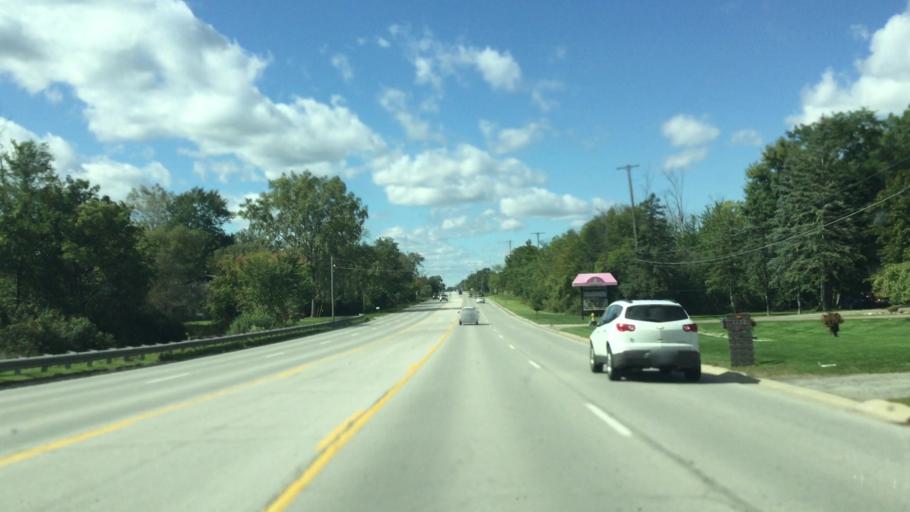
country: US
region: Michigan
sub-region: Genesee County
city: Flint
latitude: 42.9439
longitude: -83.7381
